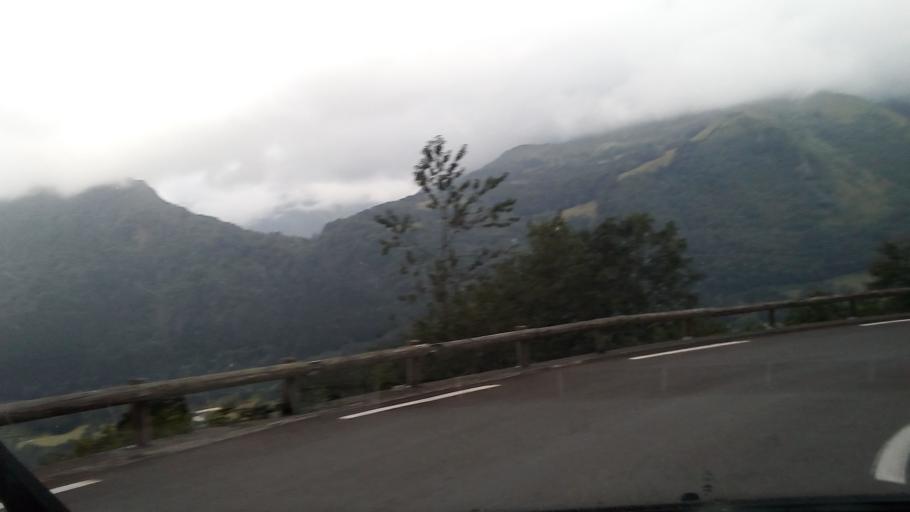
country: FR
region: Midi-Pyrenees
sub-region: Departement des Hautes-Pyrenees
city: Argeles-Gazost
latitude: 42.9664
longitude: -0.2152
